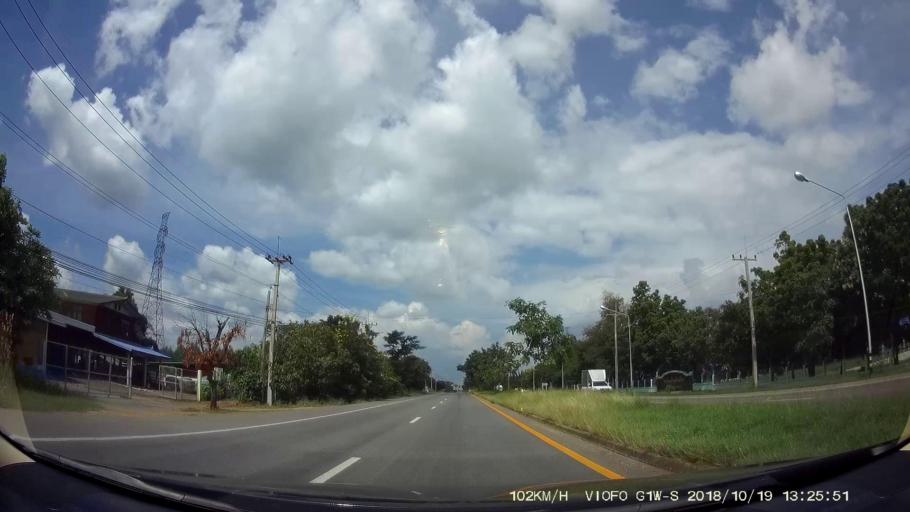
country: TH
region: Chaiyaphum
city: Chatturat
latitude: 15.5267
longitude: 101.8290
